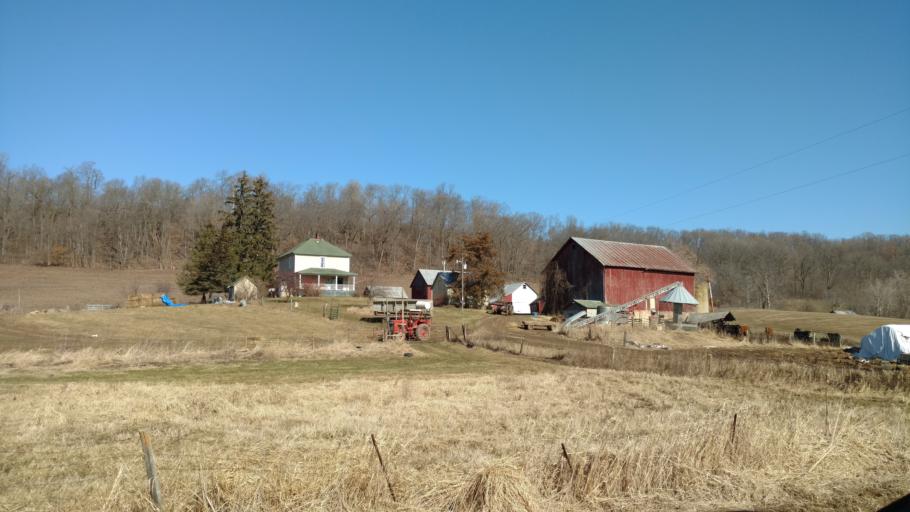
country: US
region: Wisconsin
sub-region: Vernon County
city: Hillsboro
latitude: 43.6089
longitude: -90.3657
